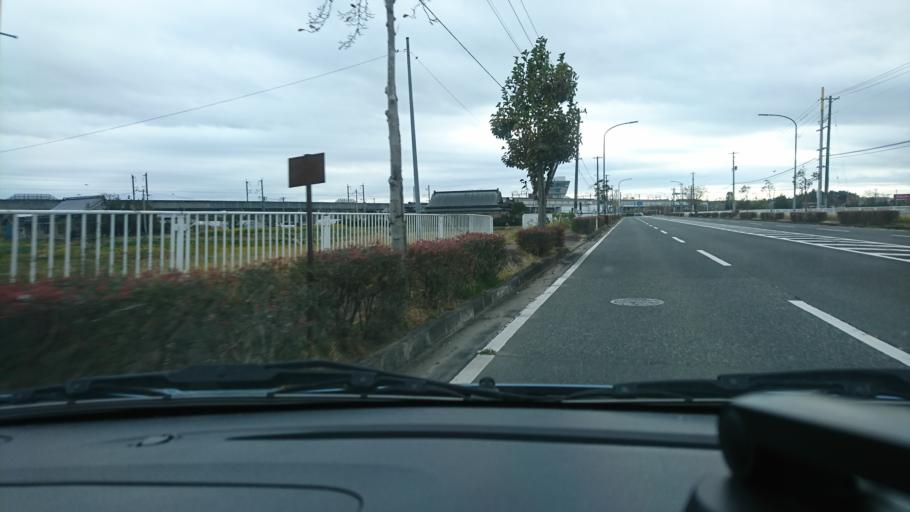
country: JP
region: Iwate
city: Ichinoseki
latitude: 38.7531
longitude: 141.0715
